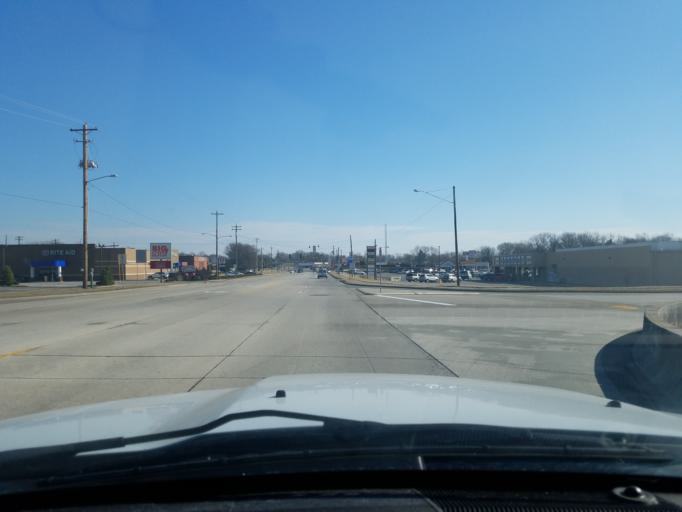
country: US
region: Kentucky
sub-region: Henderson County
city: Henderson
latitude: 37.8333
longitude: -87.5734
